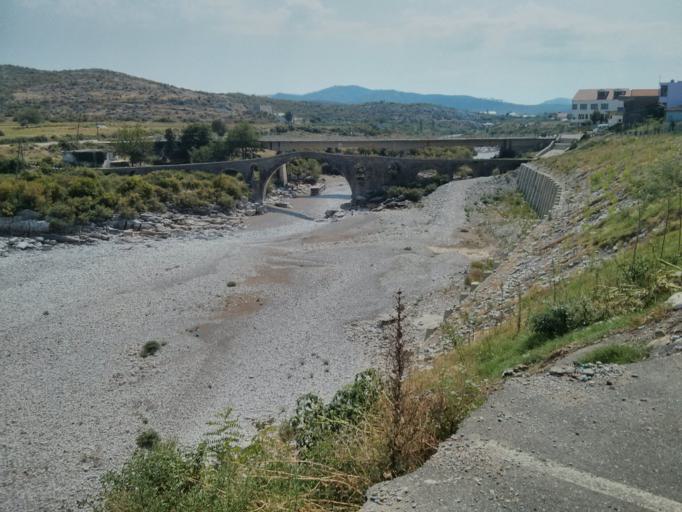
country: AL
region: Shkoder
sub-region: Rrethi i Malesia e Madhe
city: Gruemire
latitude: 42.1158
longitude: 19.5747
